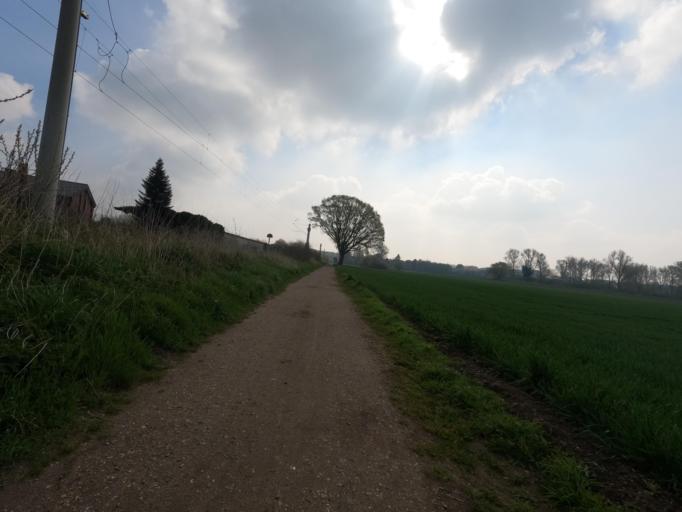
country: DE
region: North Rhine-Westphalia
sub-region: Regierungsbezirk Koln
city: Heinsberg
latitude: 51.0556
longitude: 6.1279
